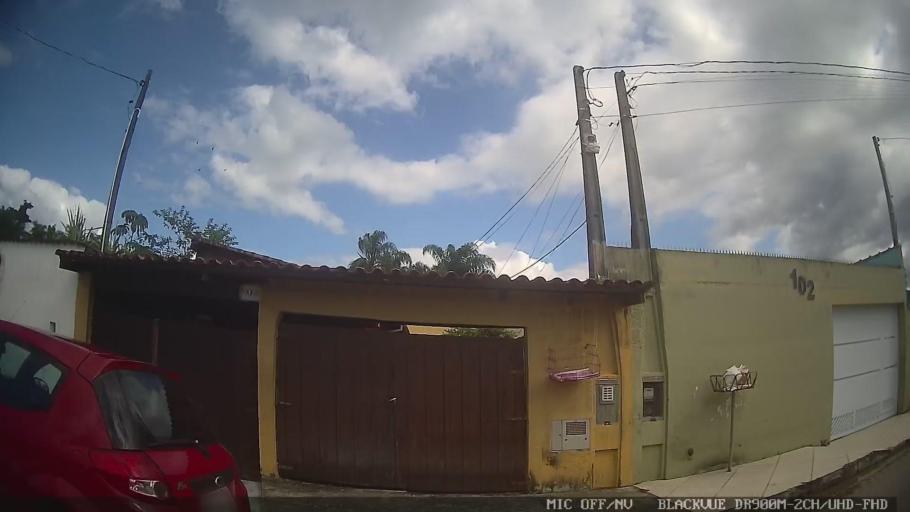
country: BR
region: Sao Paulo
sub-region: Sao Sebastiao
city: Sao Sebastiao
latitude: -23.7177
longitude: -45.4252
